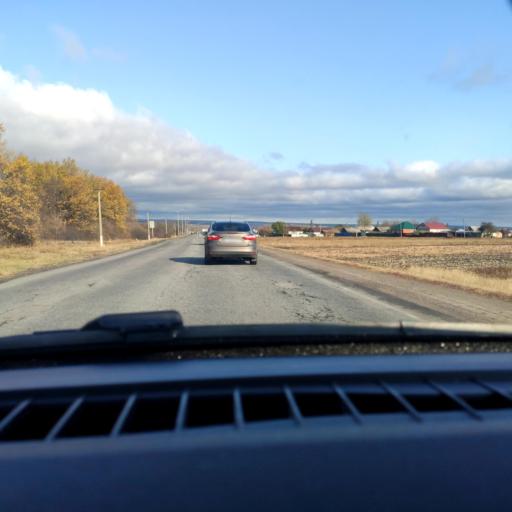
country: RU
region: Belgorod
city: Ilovka
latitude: 50.7245
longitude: 38.6812
